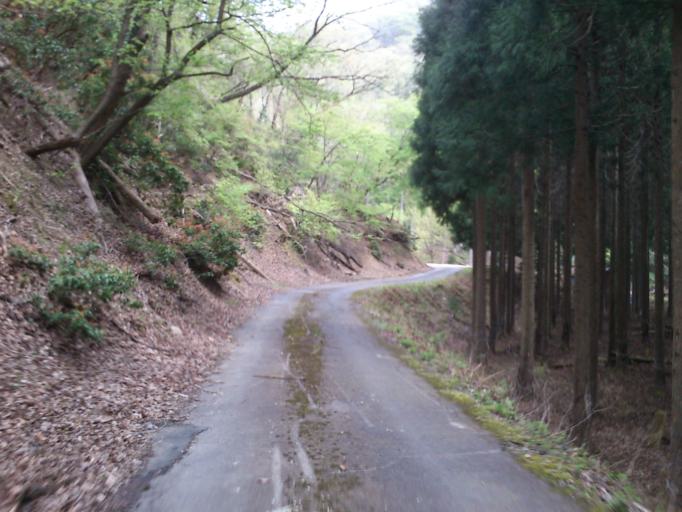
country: JP
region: Kyoto
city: Maizuru
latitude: 35.3987
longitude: 135.5021
